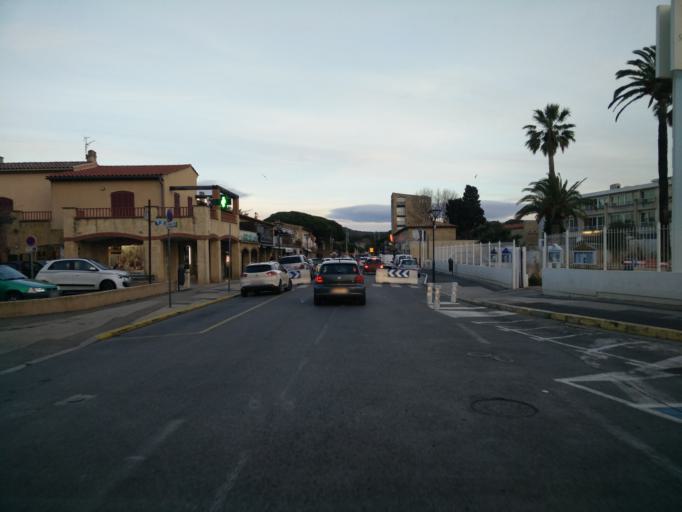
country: FR
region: Provence-Alpes-Cote d'Azur
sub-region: Departement du Var
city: La Seyne-sur-Mer
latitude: 43.0794
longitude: 5.8922
